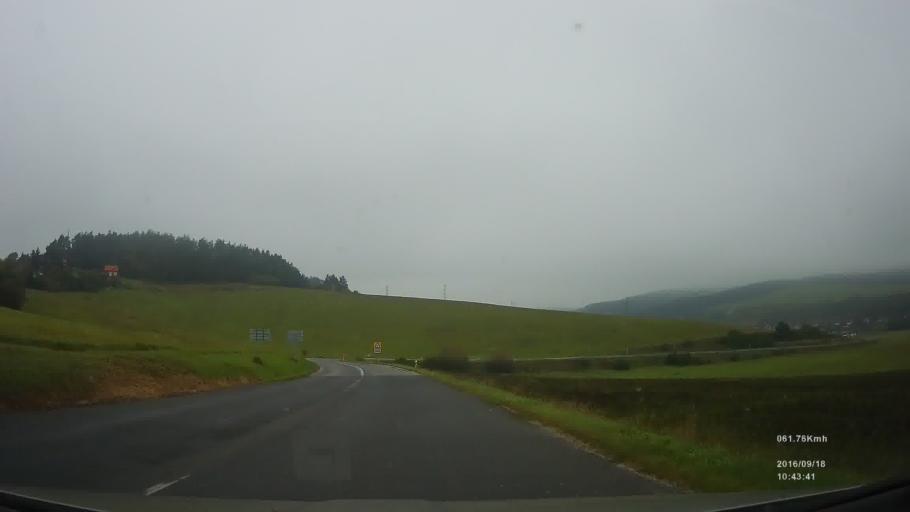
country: SK
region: Kosicky
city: Spisska Nova Ves
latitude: 48.9504
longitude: 20.5804
